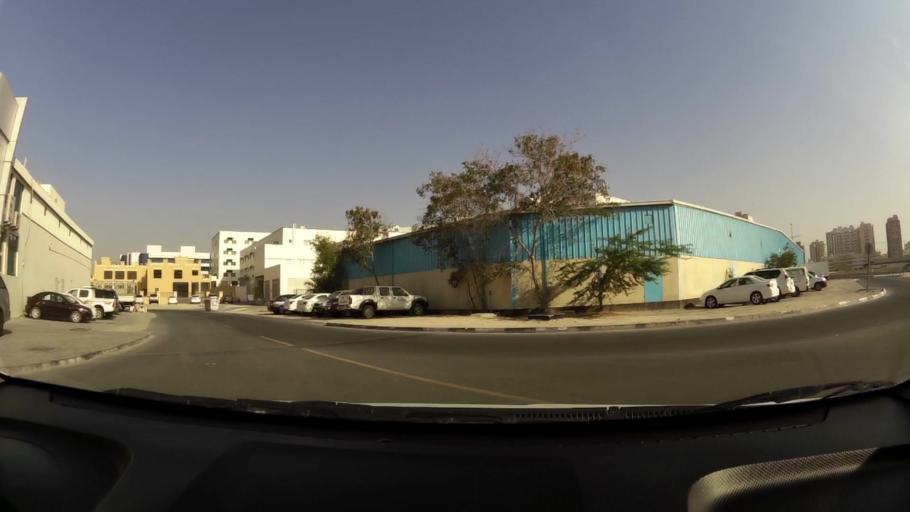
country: AE
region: Ash Shariqah
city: Sharjah
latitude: 25.2795
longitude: 55.3839
